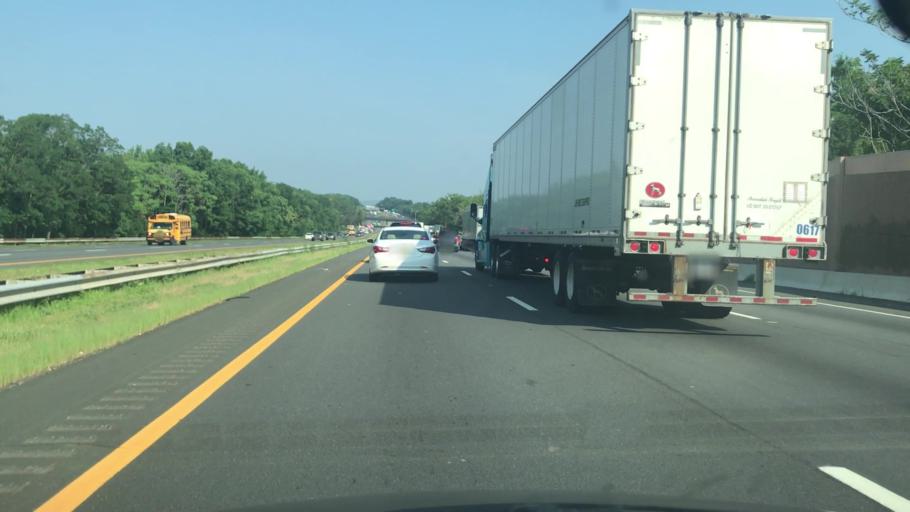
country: US
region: New Jersey
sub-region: Middlesex County
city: Metuchen
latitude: 40.5374
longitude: -74.3830
